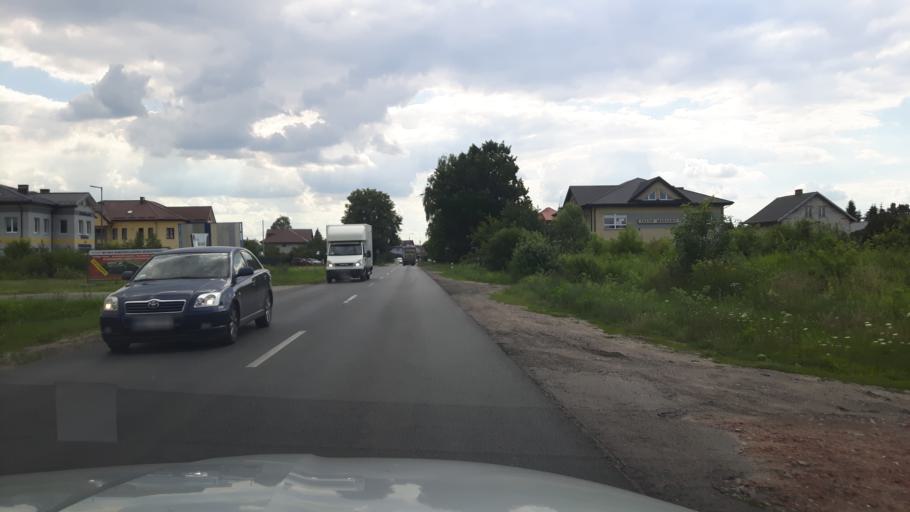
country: PL
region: Masovian Voivodeship
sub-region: Powiat wolominski
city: Wolomin
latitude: 52.3406
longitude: 21.2545
